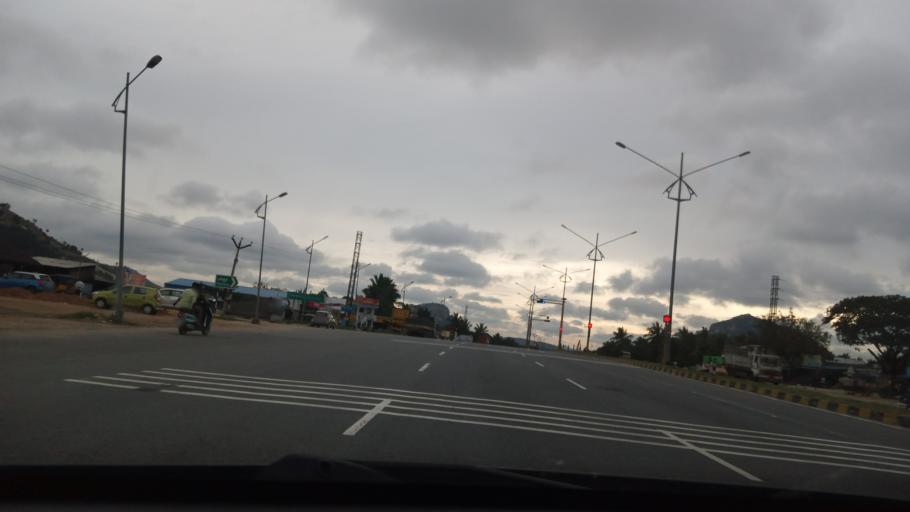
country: IN
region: Tamil Nadu
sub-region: Vellore
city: Jolarpettai
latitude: 12.5730
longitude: 78.4784
